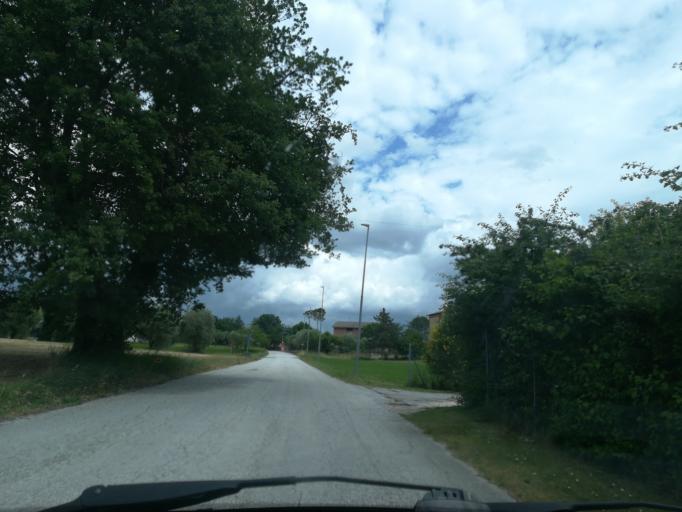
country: IT
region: The Marches
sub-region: Provincia di Macerata
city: Petriolo
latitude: 43.2257
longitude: 13.4763
